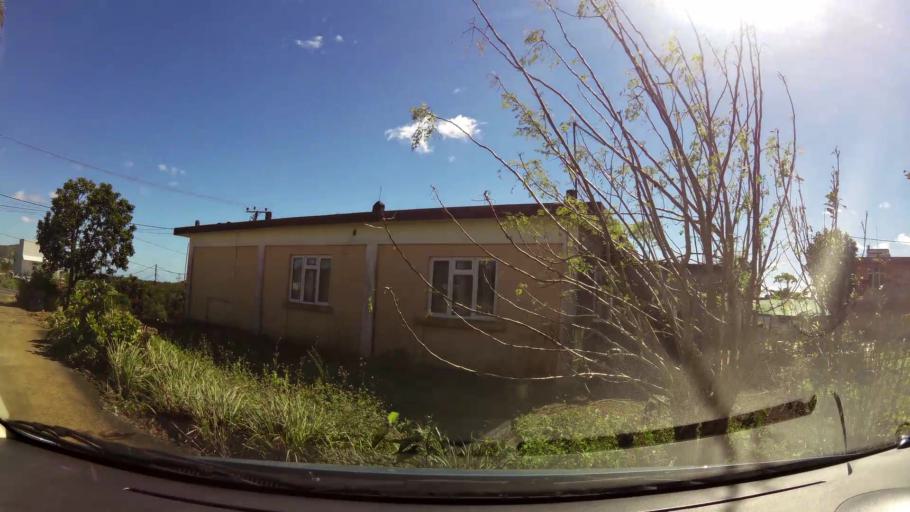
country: MU
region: Plaines Wilhems
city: Curepipe
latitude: -20.3419
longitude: 57.4931
